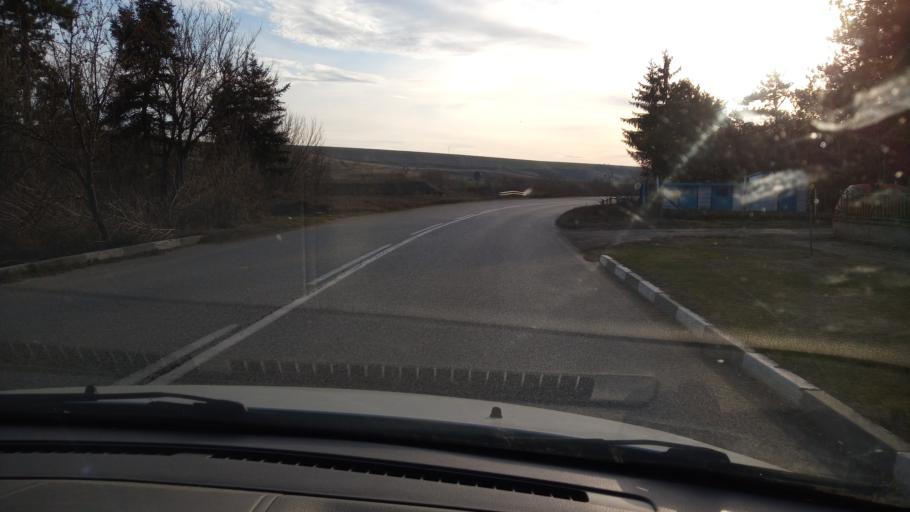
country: BG
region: Pleven
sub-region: Obshtina Pleven
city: Slavyanovo
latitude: 43.5487
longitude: 24.8623
